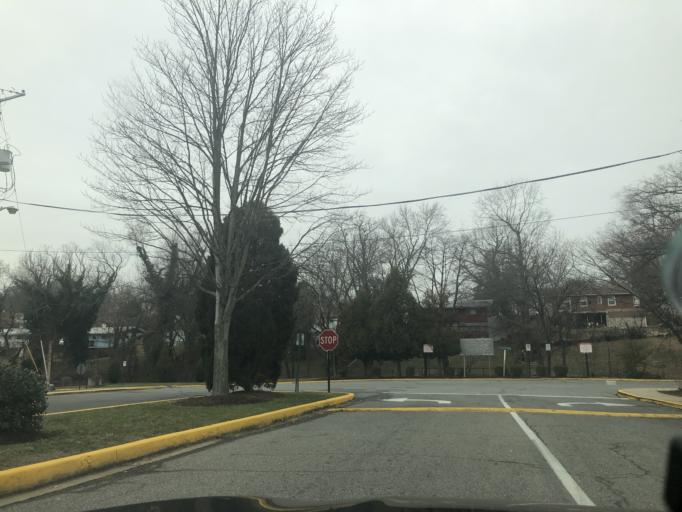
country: US
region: Maryland
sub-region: Prince George's County
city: Oxon Hill
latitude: 38.7873
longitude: -76.9991
